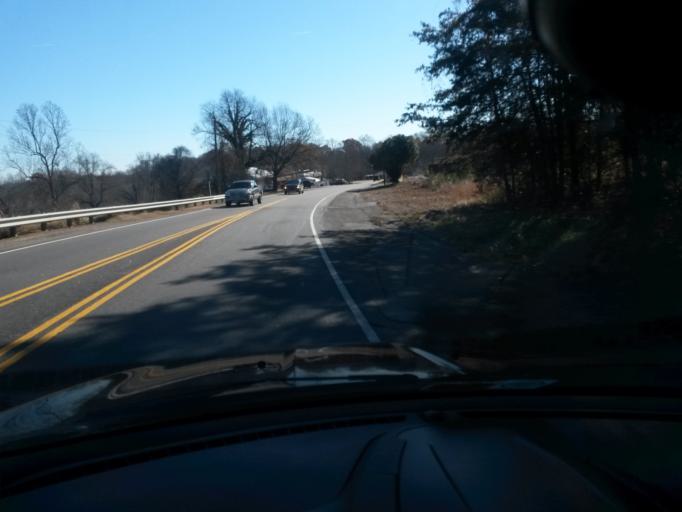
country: US
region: Virginia
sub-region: Henry County
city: Bassett
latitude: 36.7625
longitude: -80.0240
